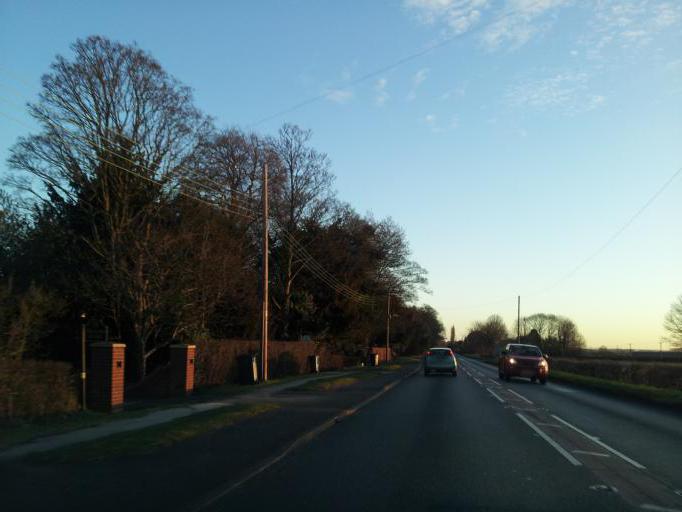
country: GB
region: England
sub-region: Lincolnshire
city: Sudbrooke
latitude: 53.2655
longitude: -0.4406
